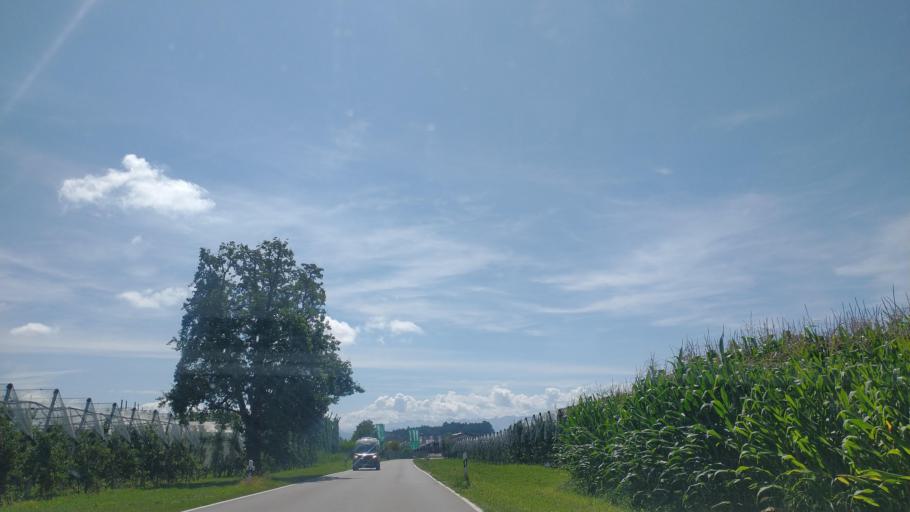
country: DE
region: Baden-Wuerttemberg
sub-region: Tuebingen Region
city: Kressbronn am Bodensee
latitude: 47.6071
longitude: 9.5943
